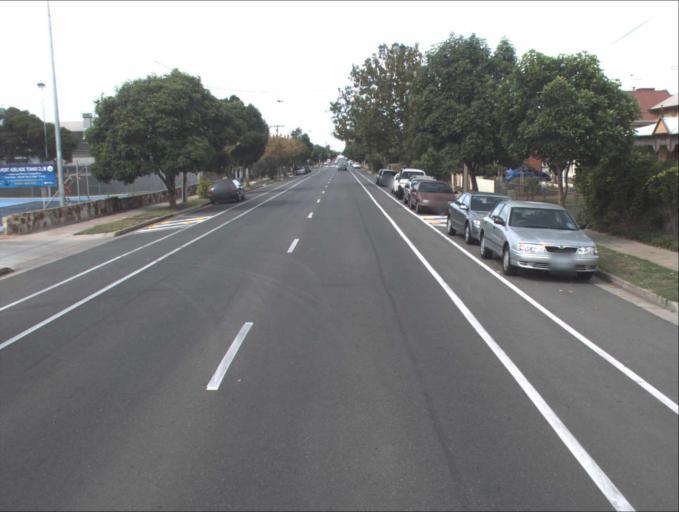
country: AU
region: South Australia
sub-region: Port Adelaide Enfield
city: Birkenhead
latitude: -34.8322
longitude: 138.4875
